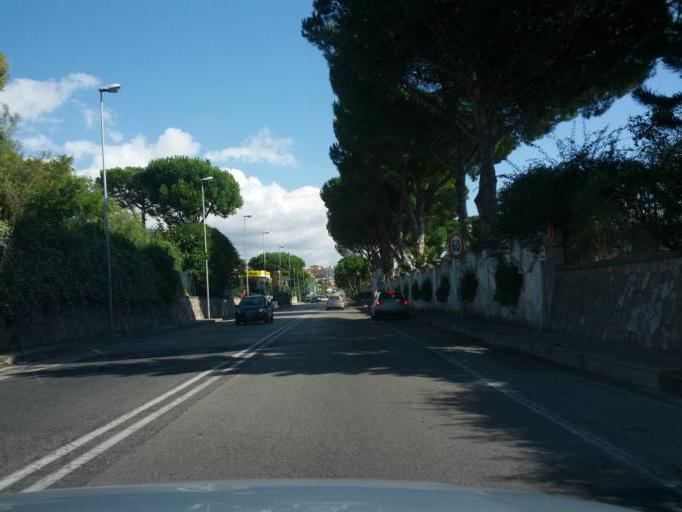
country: IT
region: Latium
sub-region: Provincia di Latina
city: Gaeta
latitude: 41.2496
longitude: 13.5877
